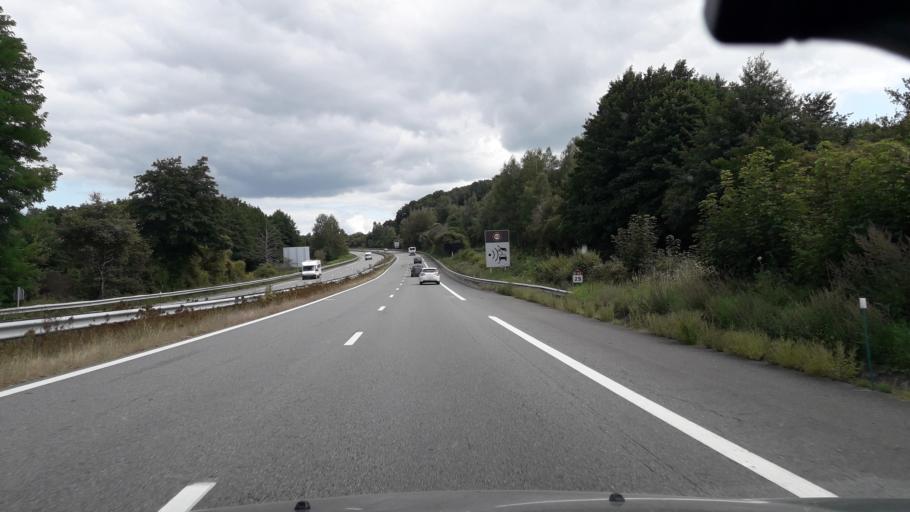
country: FR
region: Limousin
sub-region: Departement de la Creuse
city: Saint-Vaury
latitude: 46.2185
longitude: 1.7073
